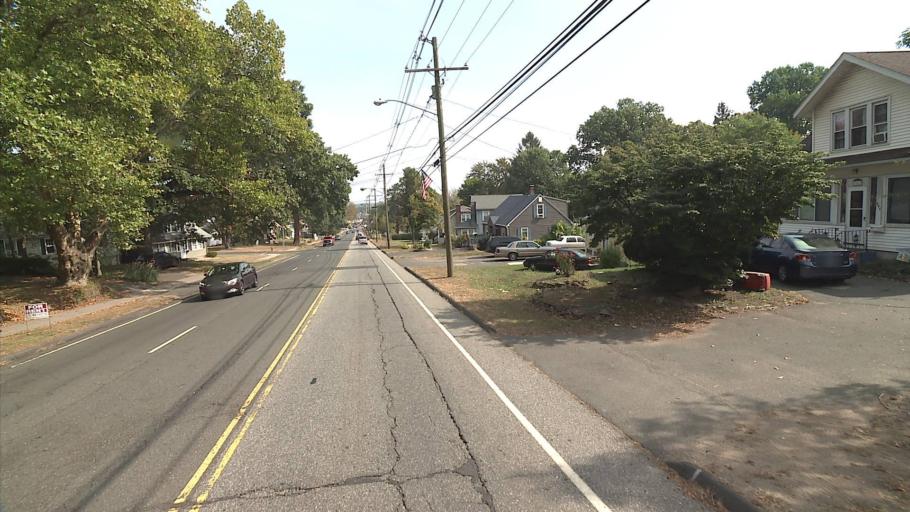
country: US
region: Connecticut
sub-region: Hartford County
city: Bristol
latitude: 41.6879
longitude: -72.9324
